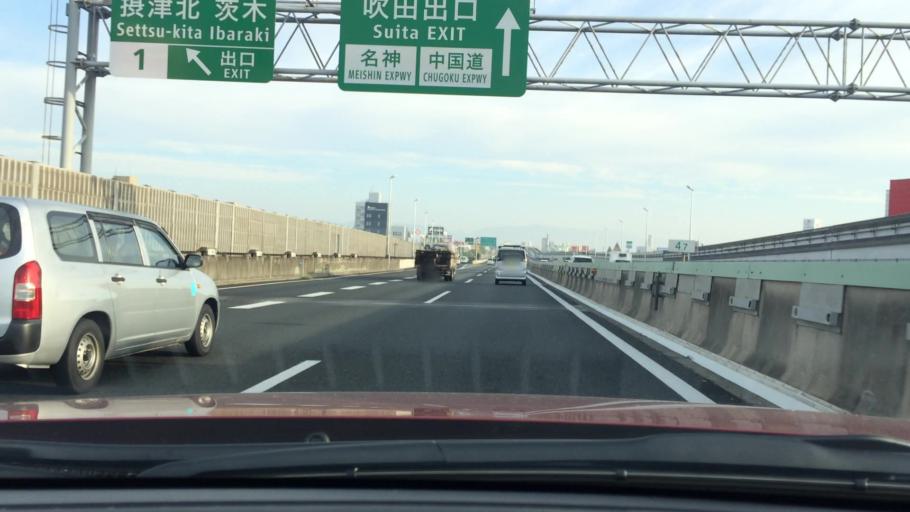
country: JP
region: Osaka
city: Ibaraki
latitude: 34.7818
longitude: 135.5616
